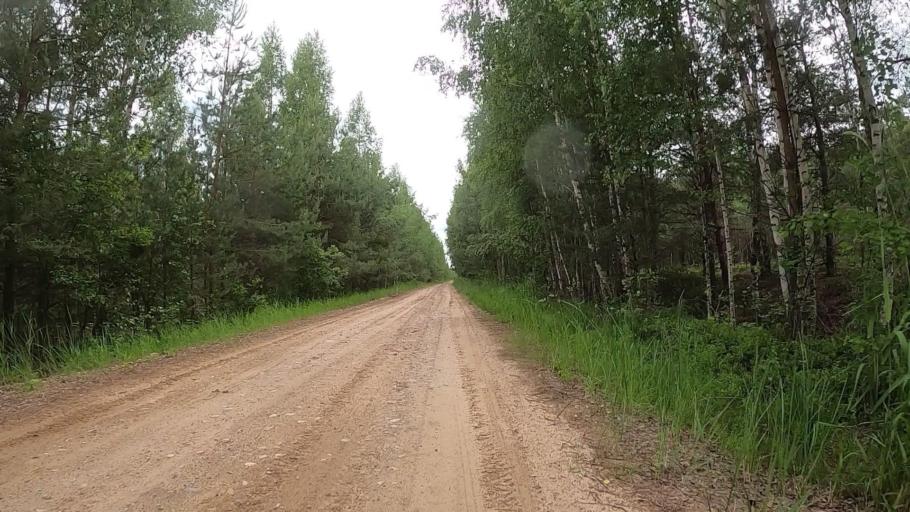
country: LV
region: Olaine
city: Olaine
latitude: 56.8443
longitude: 23.9349
